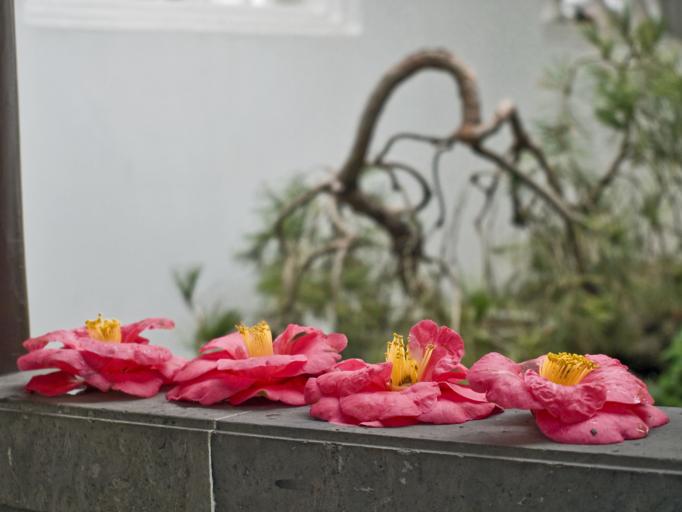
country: US
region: Oregon
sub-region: Multnomah County
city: Portland
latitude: 45.5255
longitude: -122.6728
